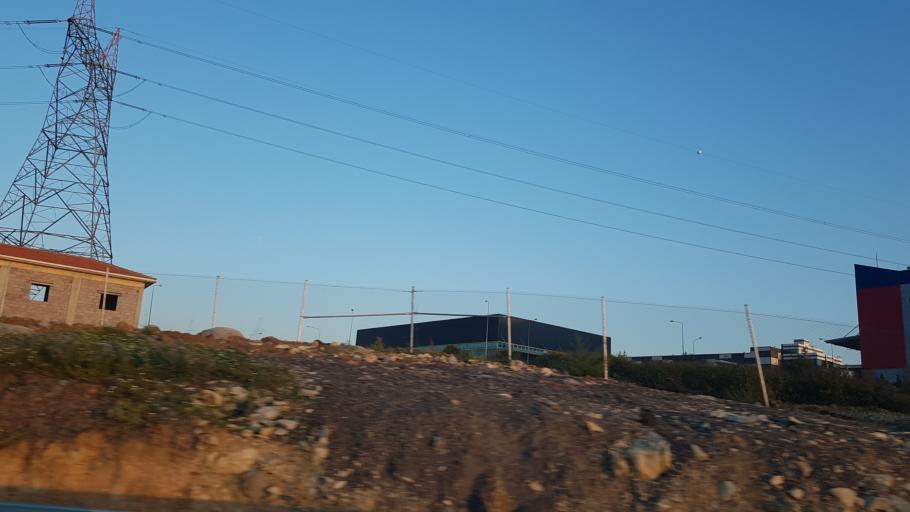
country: TR
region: Kocaeli
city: Tavsanli
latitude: 40.8017
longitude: 29.5191
